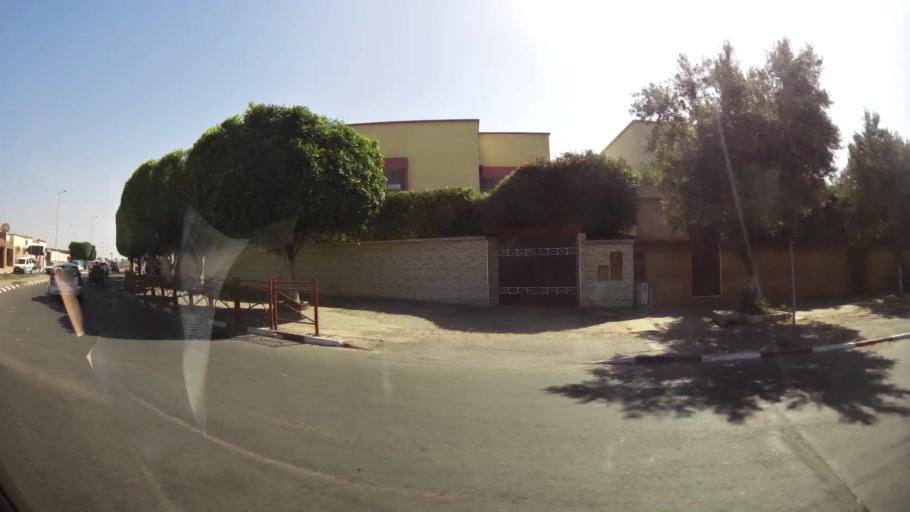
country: MA
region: Souss-Massa-Draa
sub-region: Inezgane-Ait Mellou
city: Inezgane
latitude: 30.3660
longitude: -9.5457
